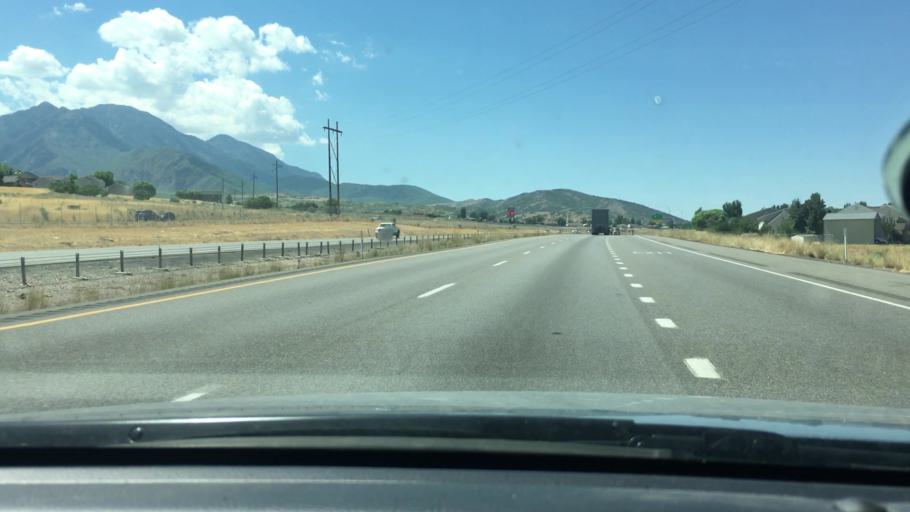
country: US
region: Utah
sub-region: Utah County
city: Santaquin
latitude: 39.9824
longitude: -111.7672
